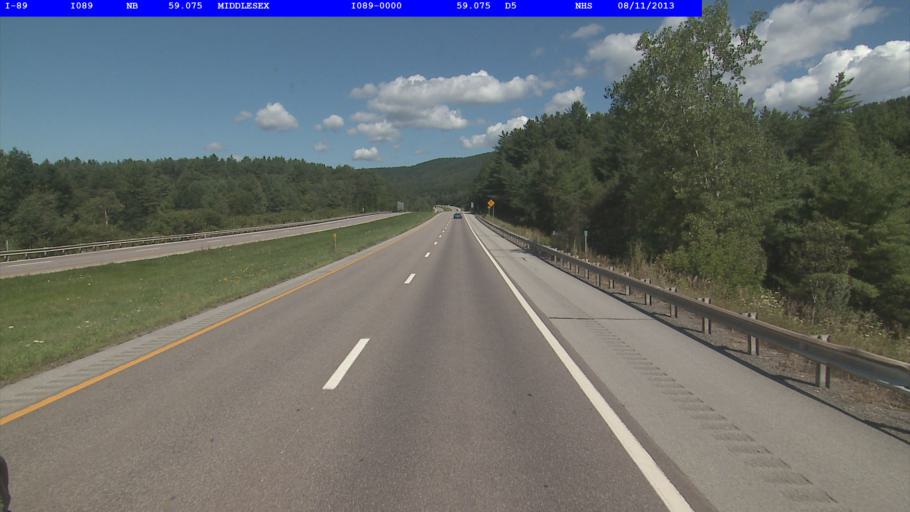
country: US
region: Vermont
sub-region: Washington County
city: Waterbury
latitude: 44.3025
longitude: -72.6890
